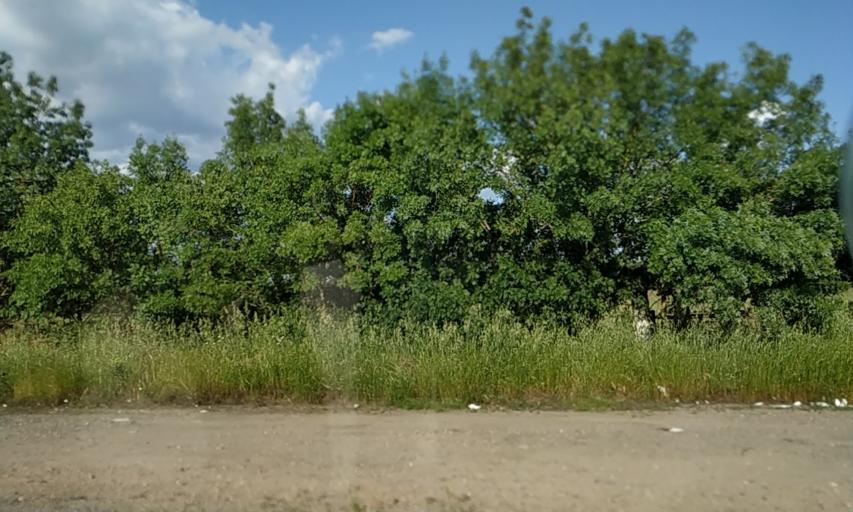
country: PT
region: Portalegre
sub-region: Portalegre
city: Urra
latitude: 39.1609
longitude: -7.4541
